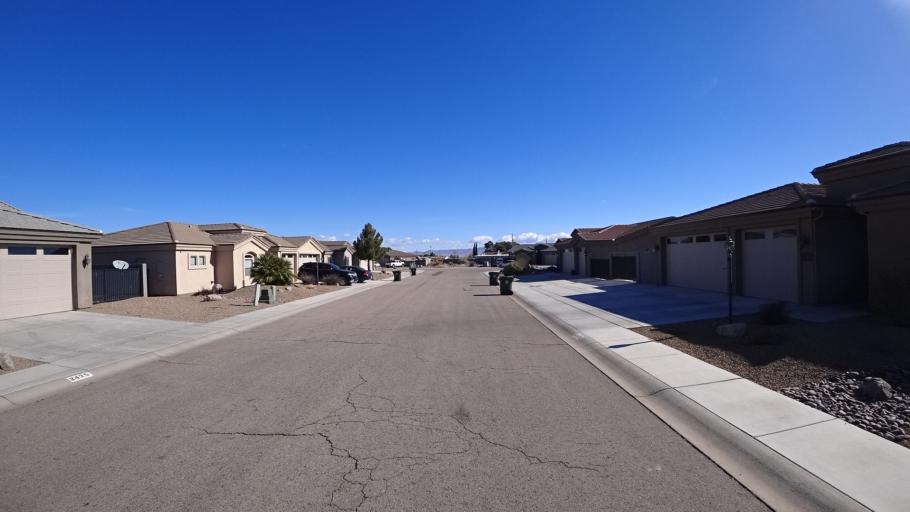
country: US
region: Arizona
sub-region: Mohave County
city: New Kingman-Butler
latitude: 35.2345
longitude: -114.0214
